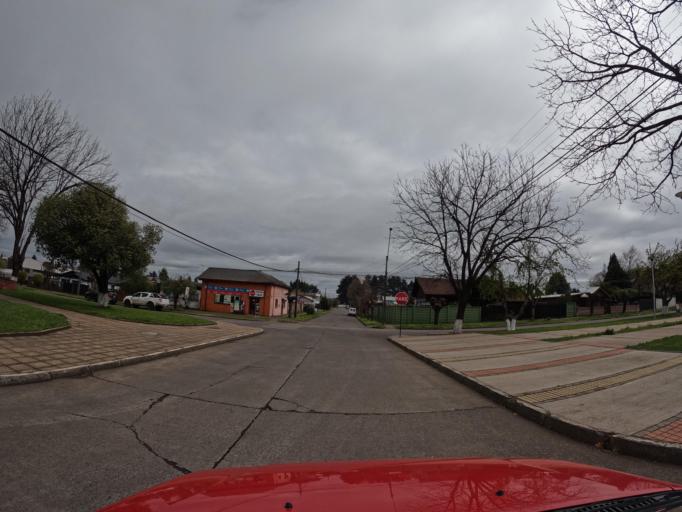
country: CL
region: Araucania
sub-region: Provincia de Malleco
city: Victoria
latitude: -38.2314
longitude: -72.3363
